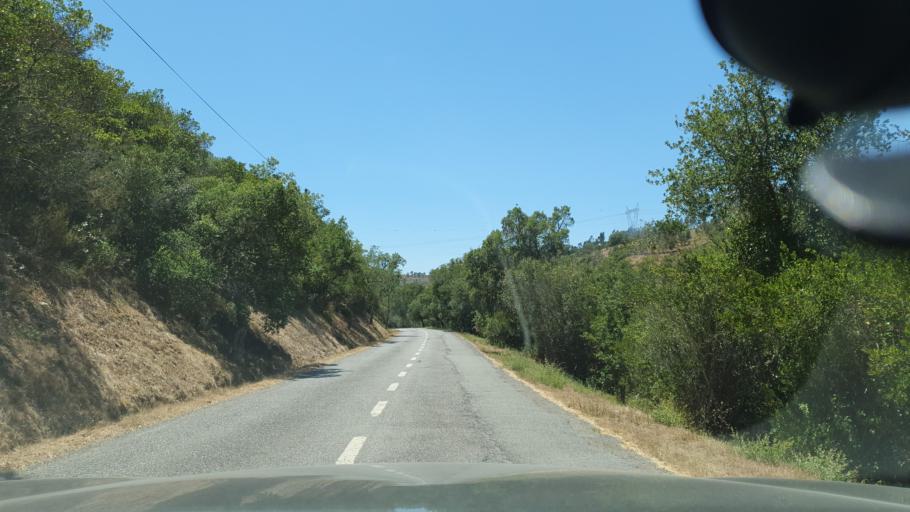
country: PT
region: Beja
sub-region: Odemira
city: Odemira
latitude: 37.6041
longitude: -8.5816
